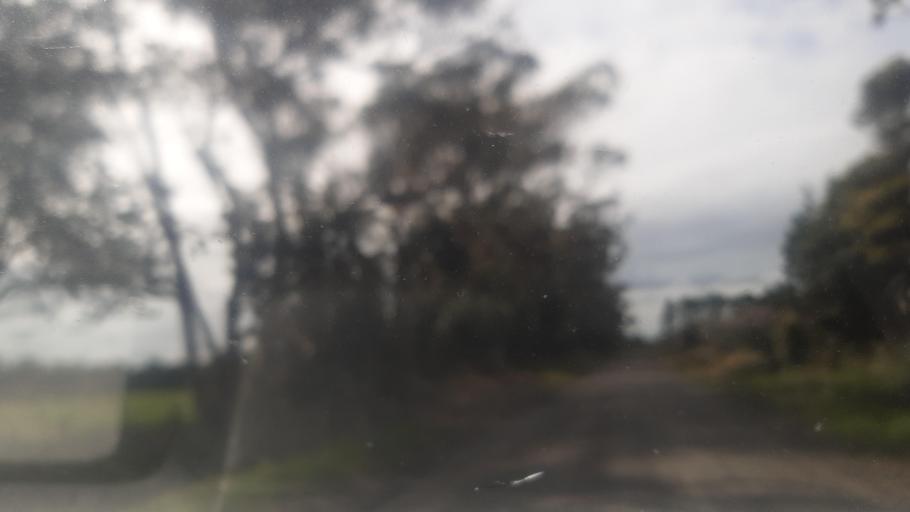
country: NZ
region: Northland
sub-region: Far North District
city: Kaitaia
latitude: -35.0445
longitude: 173.2240
